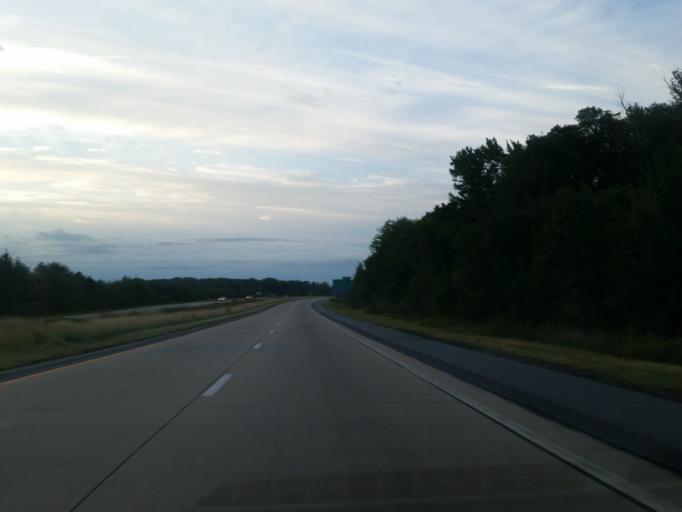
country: US
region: Delaware
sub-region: Kent County
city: Cheswold
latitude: 39.2133
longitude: -75.5519
